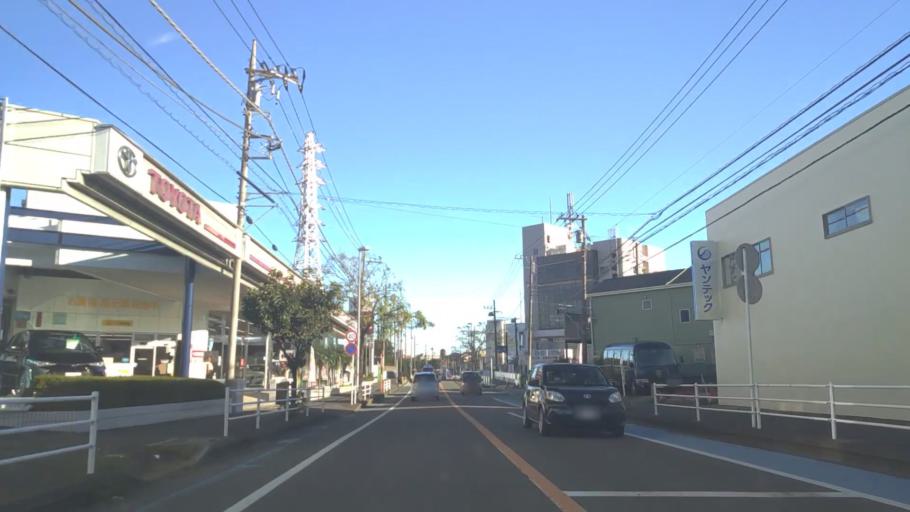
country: JP
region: Kanagawa
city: Chigasaki
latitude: 35.3397
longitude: 139.4012
